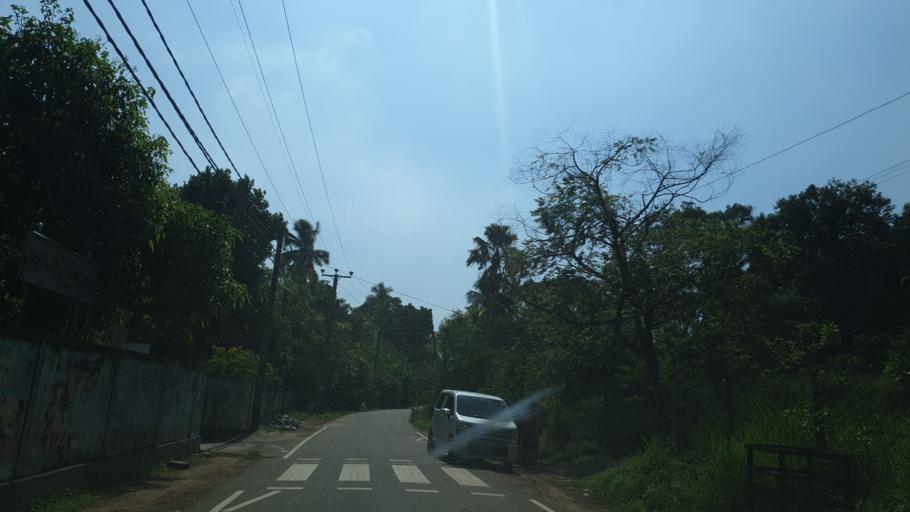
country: LK
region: Western
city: Moratuwa
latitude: 6.7643
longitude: 79.9303
